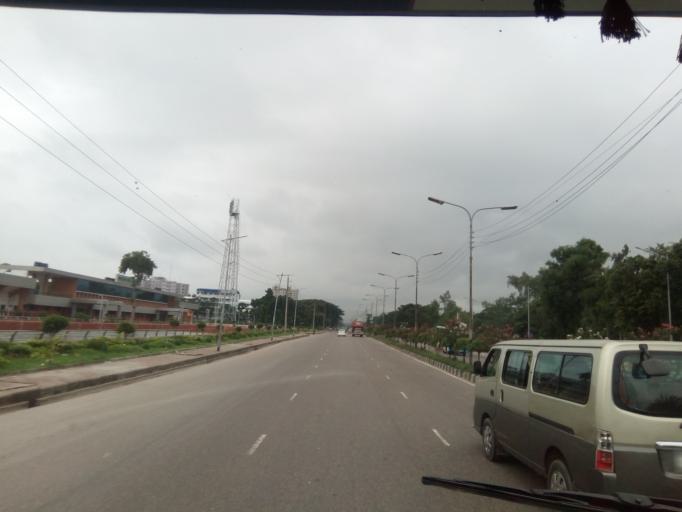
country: BD
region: Dhaka
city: Paltan
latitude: 23.8068
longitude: 90.4031
